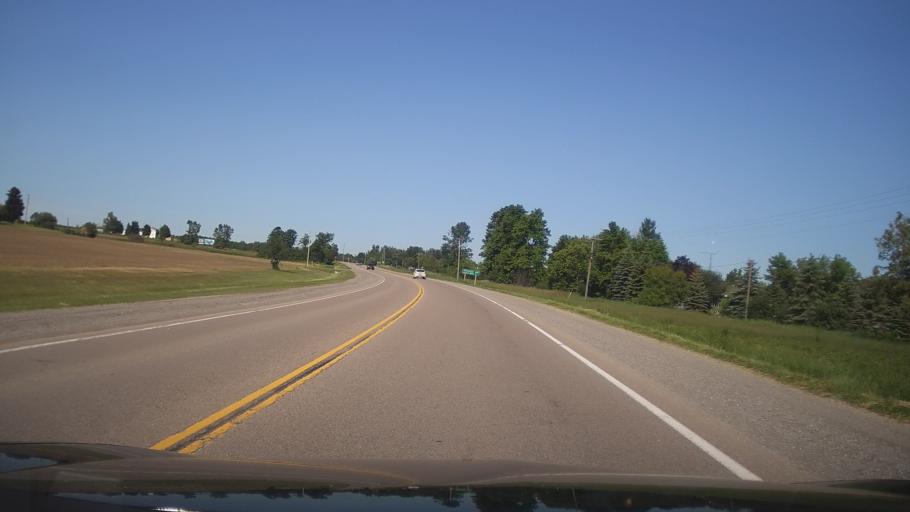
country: CA
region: Ontario
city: Omemee
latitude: 44.3487
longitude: -78.7890
